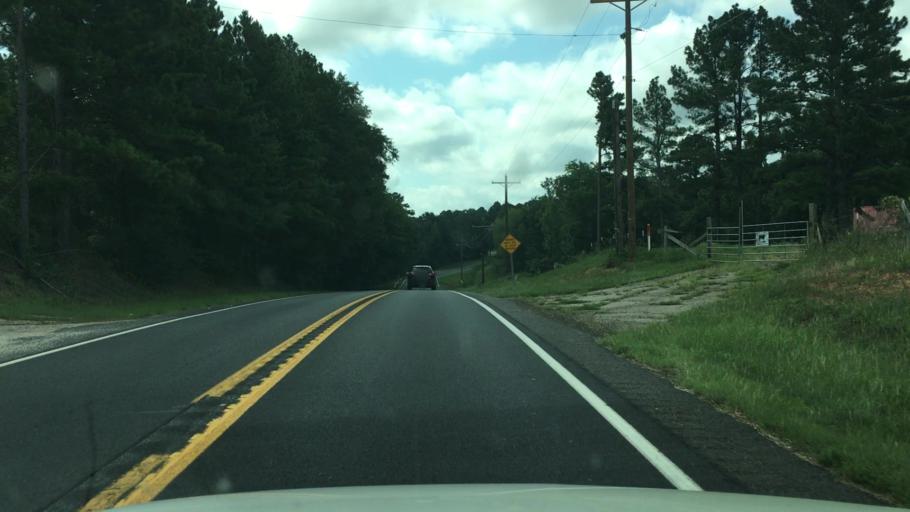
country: US
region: Arkansas
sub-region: Garland County
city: Lake Hamilton
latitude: 34.3321
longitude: -93.1761
